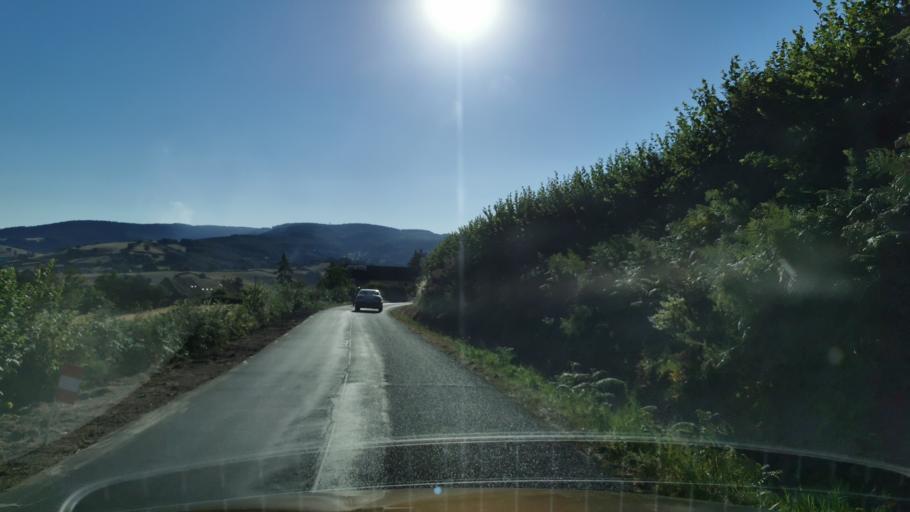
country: FR
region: Bourgogne
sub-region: Departement de Saone-et-Loire
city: Marmagne
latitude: 46.8047
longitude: 4.3416
